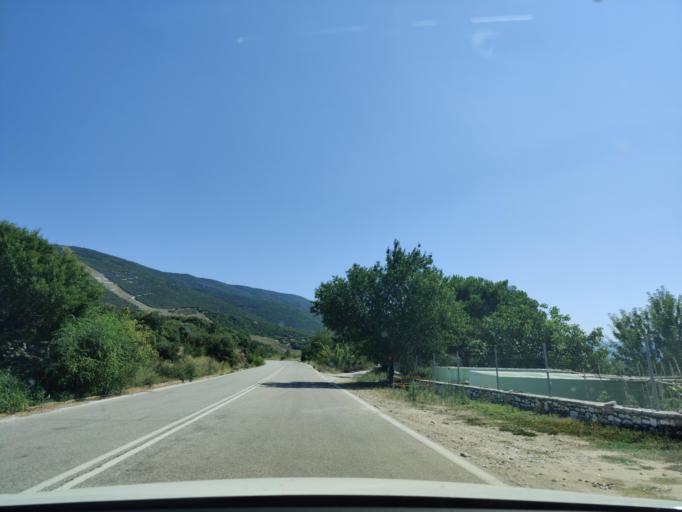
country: GR
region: East Macedonia and Thrace
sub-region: Nomos Kavalas
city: Zygos
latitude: 41.0005
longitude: 24.3801
